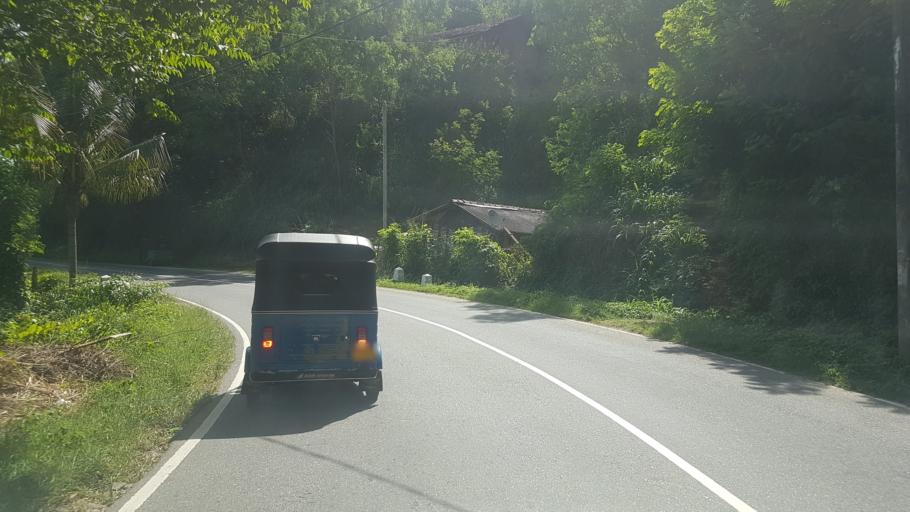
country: LK
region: Uva
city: Haputale
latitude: 6.8070
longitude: 81.0828
